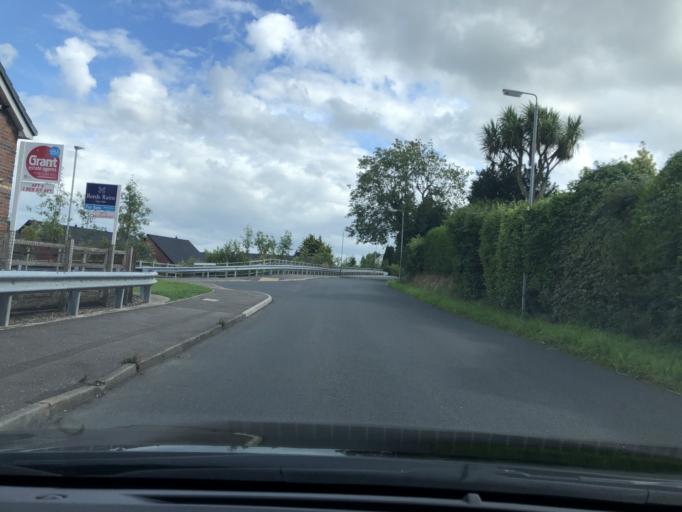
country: GB
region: Northern Ireland
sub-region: Ards District
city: Newtownards
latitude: 54.5876
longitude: -5.7138
